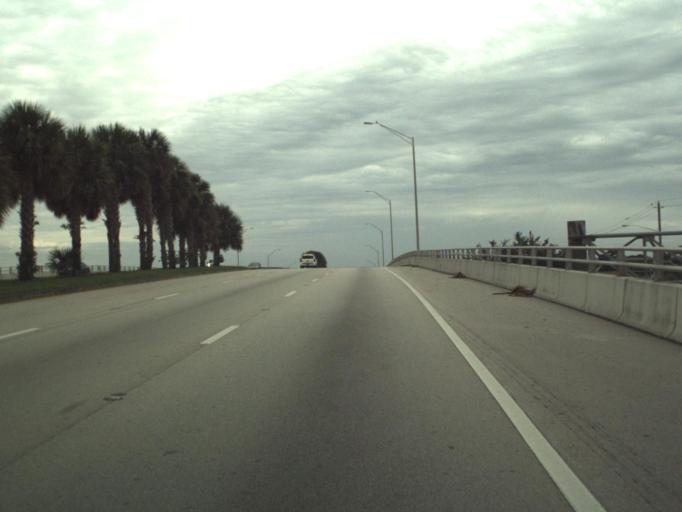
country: US
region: Florida
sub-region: Palm Beach County
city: Royal Palm Estates
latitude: 26.6782
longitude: -80.1106
